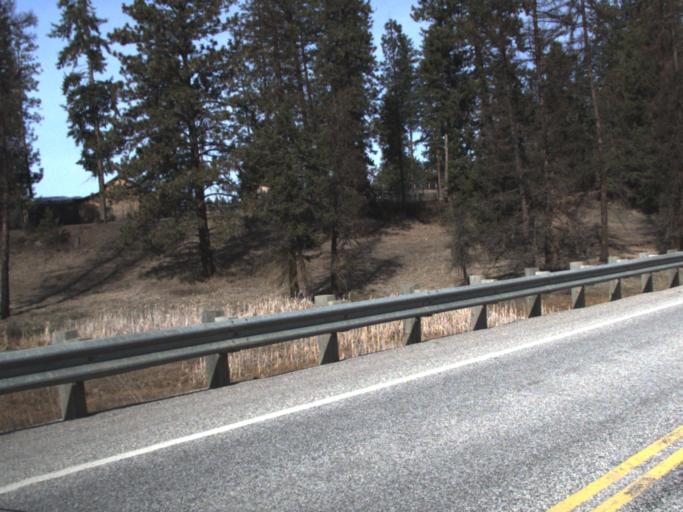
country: US
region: Washington
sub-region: Stevens County
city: Colville
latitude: 48.5165
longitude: -117.8070
